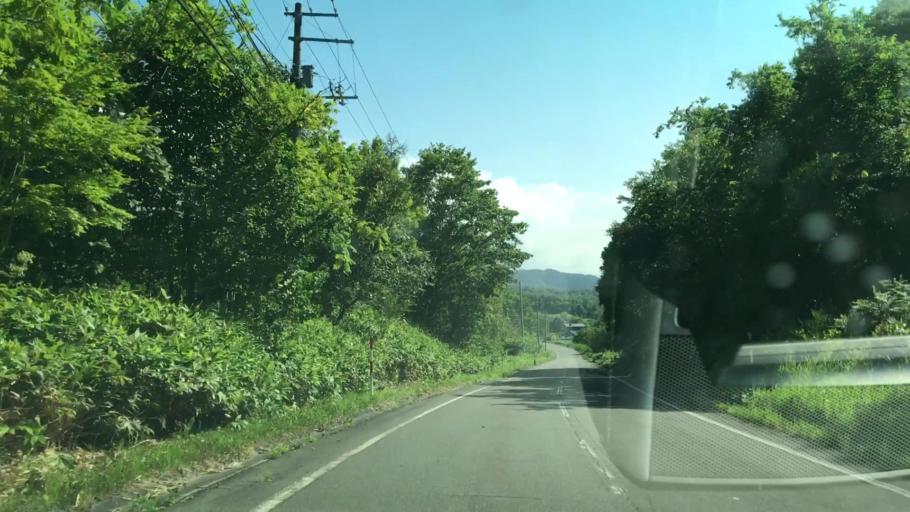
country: JP
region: Hokkaido
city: Shimo-furano
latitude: 42.8596
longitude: 142.4406
